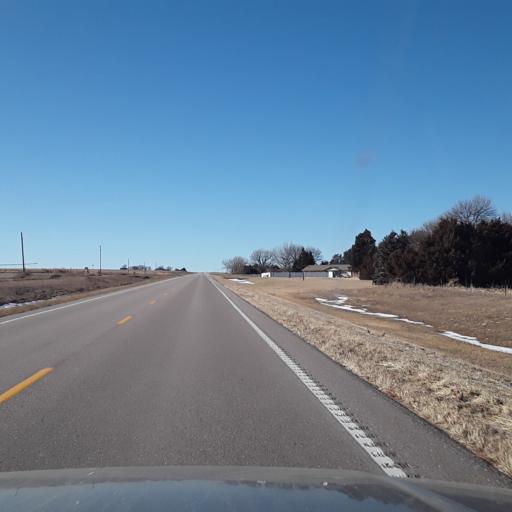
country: US
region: Nebraska
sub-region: Frontier County
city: Stockville
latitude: 40.7003
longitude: -100.2635
